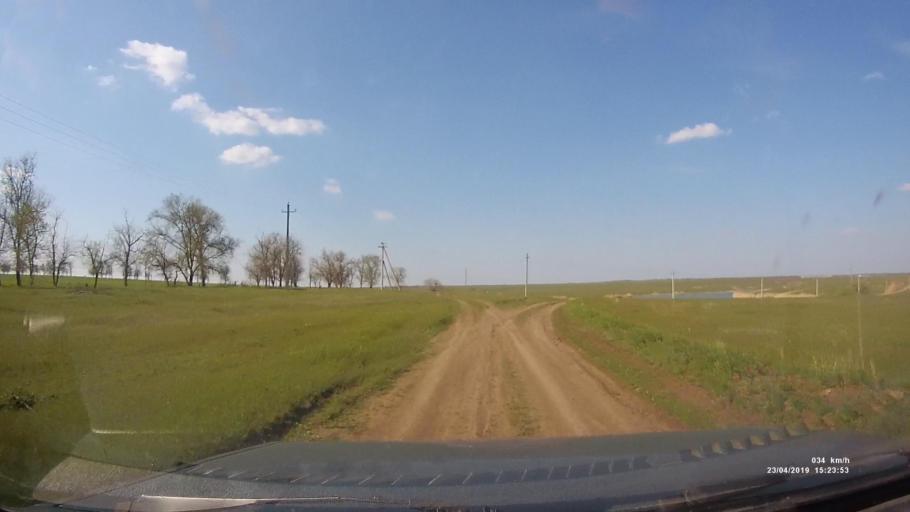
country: RU
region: Rostov
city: Remontnoye
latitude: 46.5382
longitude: 42.9697
